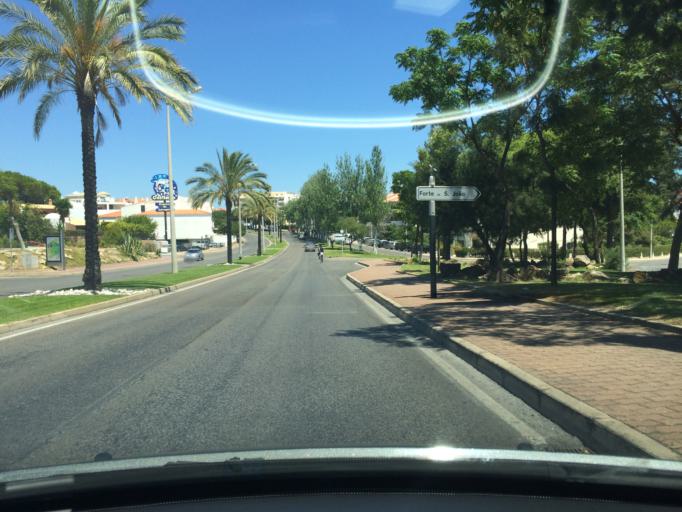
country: PT
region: Faro
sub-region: Albufeira
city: Albufeira
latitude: 37.0925
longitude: -8.2368
